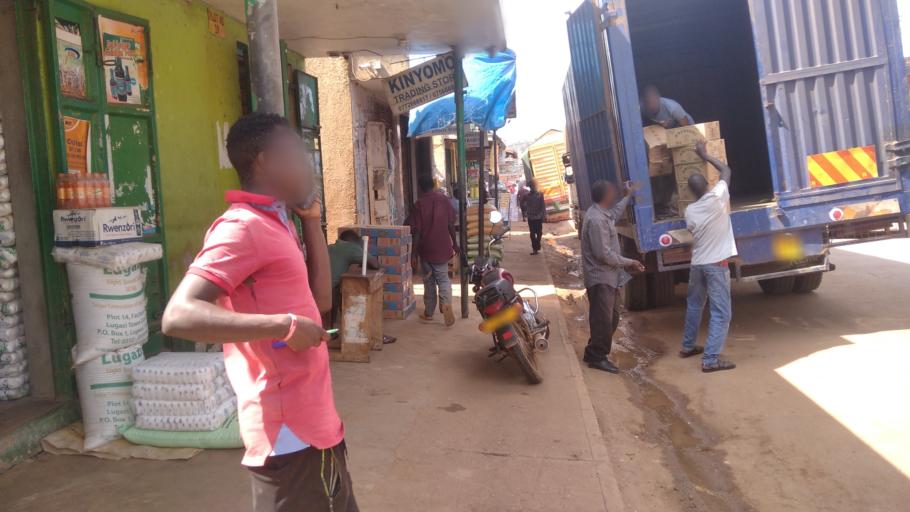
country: UG
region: Central Region
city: Masaka
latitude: -0.3429
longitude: 31.7388
